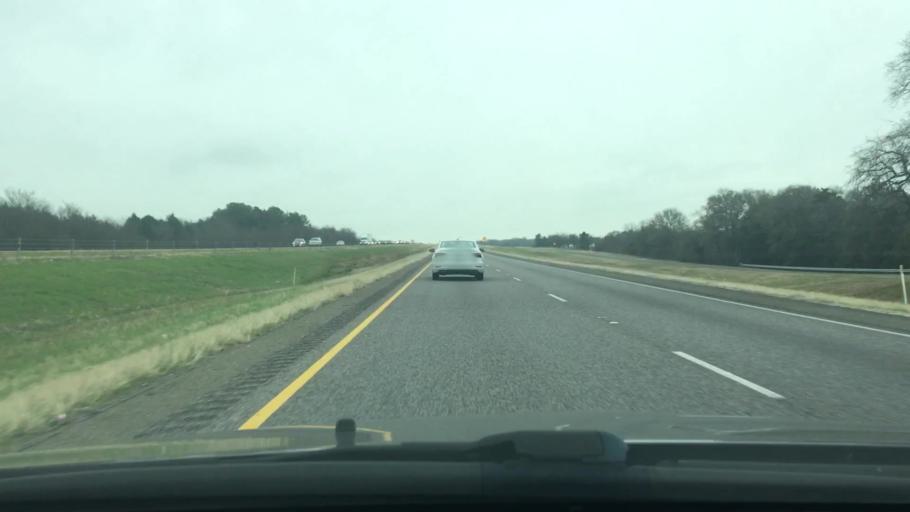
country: US
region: Texas
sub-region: Freestone County
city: Fairfield
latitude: 31.7769
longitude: -96.2280
